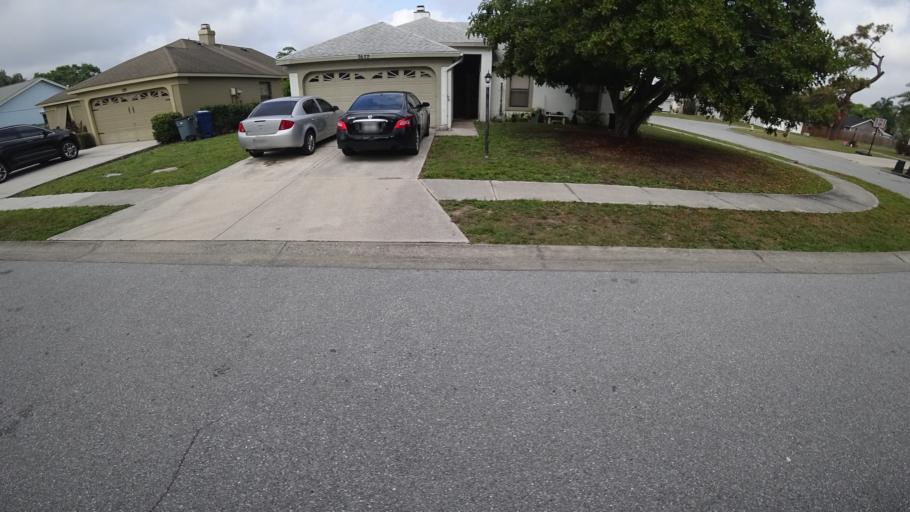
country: US
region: Florida
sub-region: Sarasota County
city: North Sarasota
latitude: 27.4048
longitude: -82.5149
